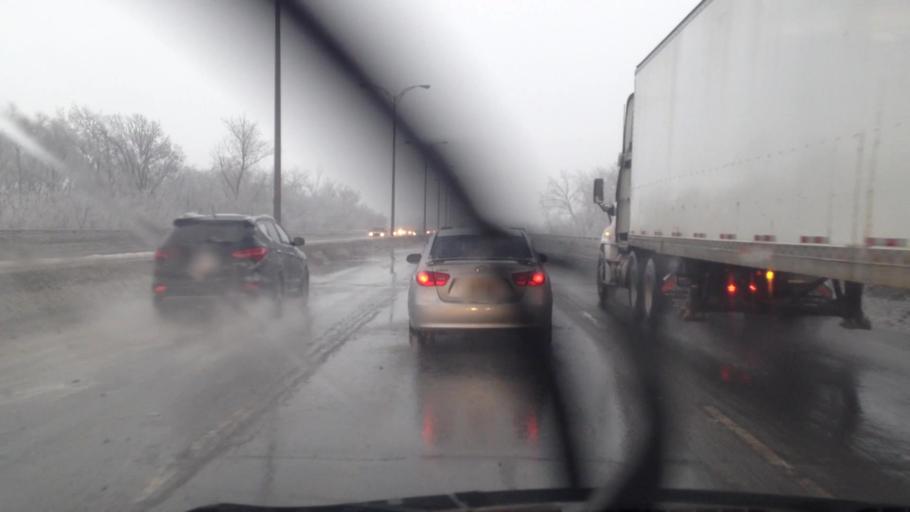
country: CA
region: Quebec
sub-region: Laurentides
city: Boisbriand
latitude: 45.6125
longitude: -73.8163
